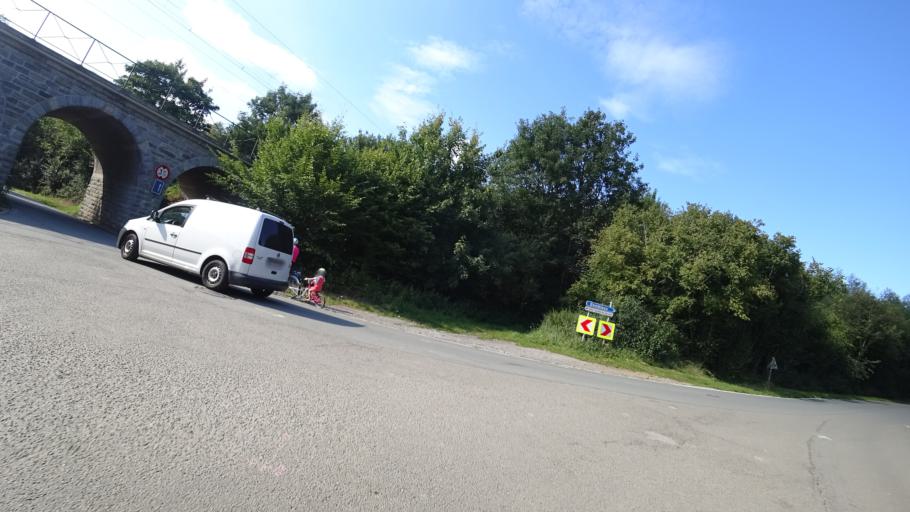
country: BE
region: Wallonia
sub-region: Province de Namur
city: Gembloux
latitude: 50.5368
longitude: 4.6892
